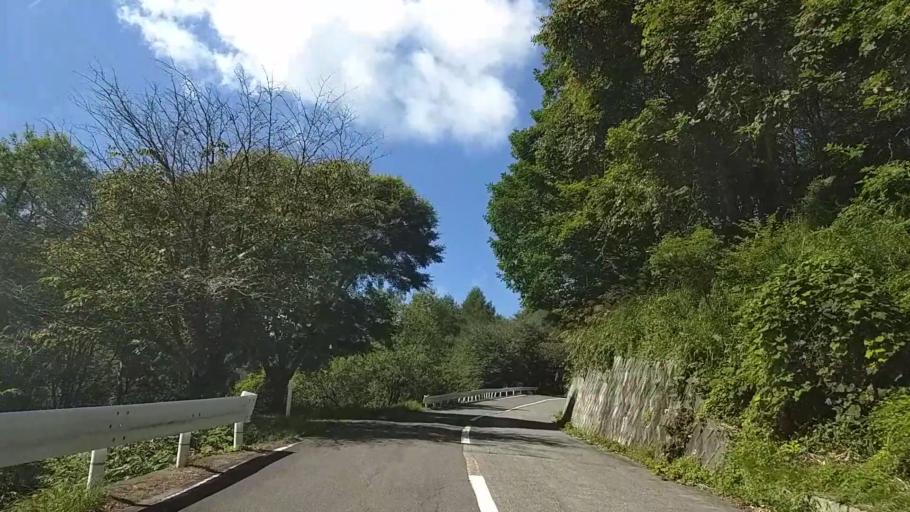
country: JP
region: Nagano
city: Suwa
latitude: 36.1945
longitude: 138.1203
